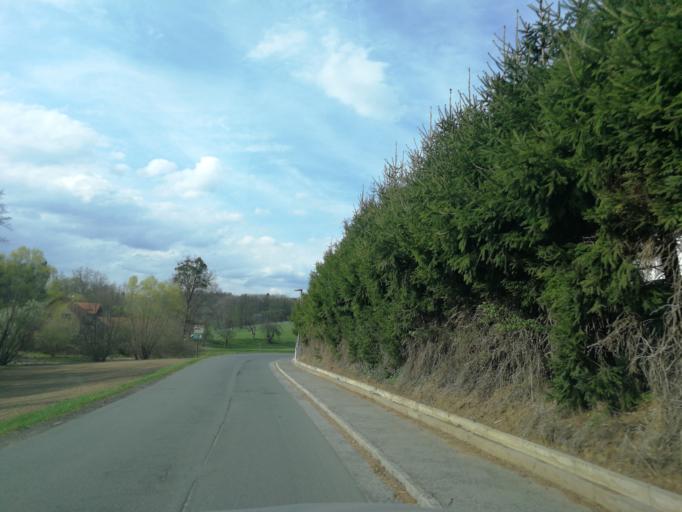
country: AT
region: Styria
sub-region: Politischer Bezirk Graz-Umgebung
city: Hart bei Graz
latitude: 47.0489
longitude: 15.5116
